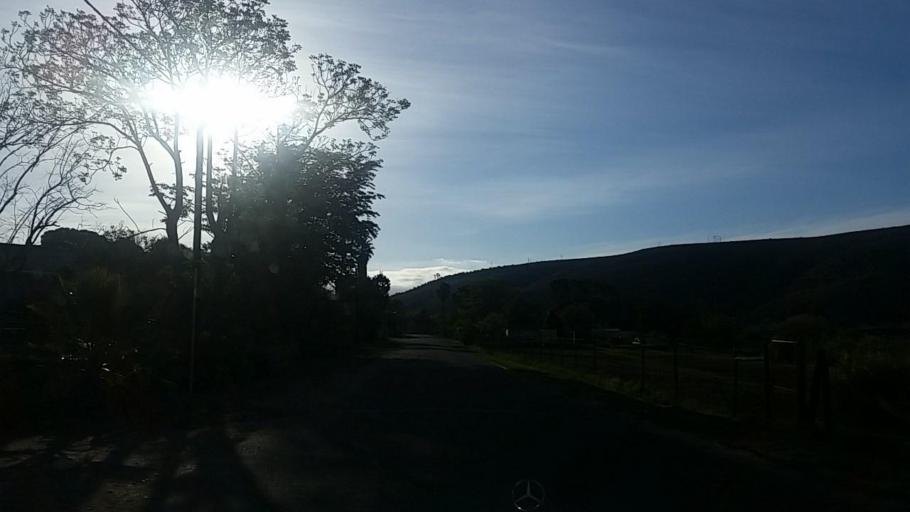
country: ZA
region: Western Cape
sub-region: Eden District Municipality
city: Knysna
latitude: -33.6541
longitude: 23.1322
